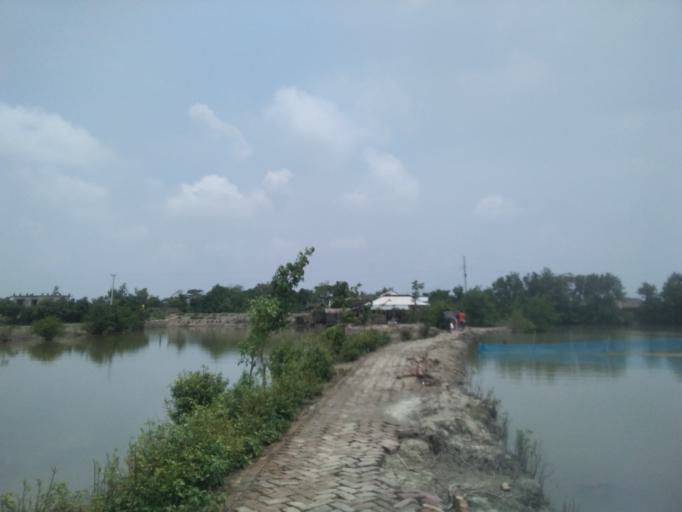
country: BD
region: Khulna
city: Phultala
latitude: 22.6400
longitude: 89.4012
